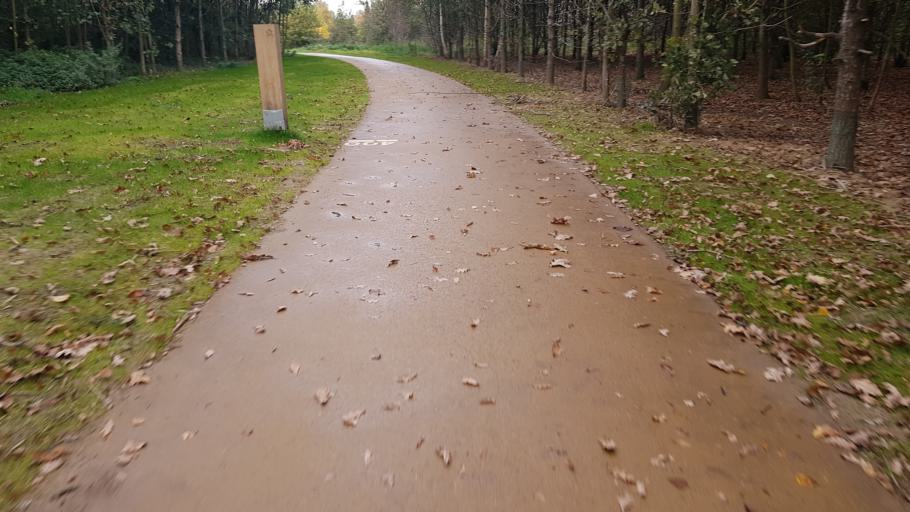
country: BE
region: Flanders
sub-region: Provincie Vlaams-Brabant
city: Wemmel
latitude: 50.8789
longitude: 4.2957
